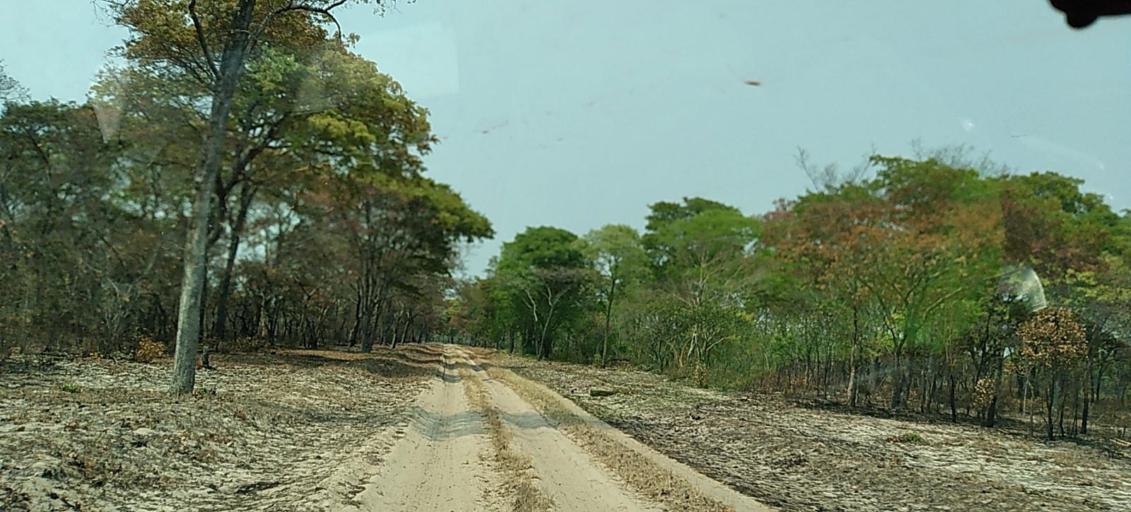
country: ZM
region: North-Western
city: Zambezi
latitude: -13.9378
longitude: 23.2221
